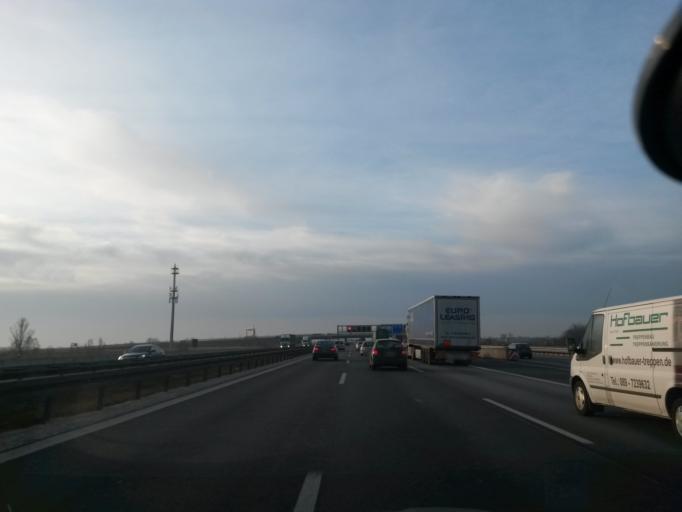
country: DE
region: Bavaria
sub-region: Upper Bavaria
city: Eching
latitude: 48.3212
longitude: 11.6180
